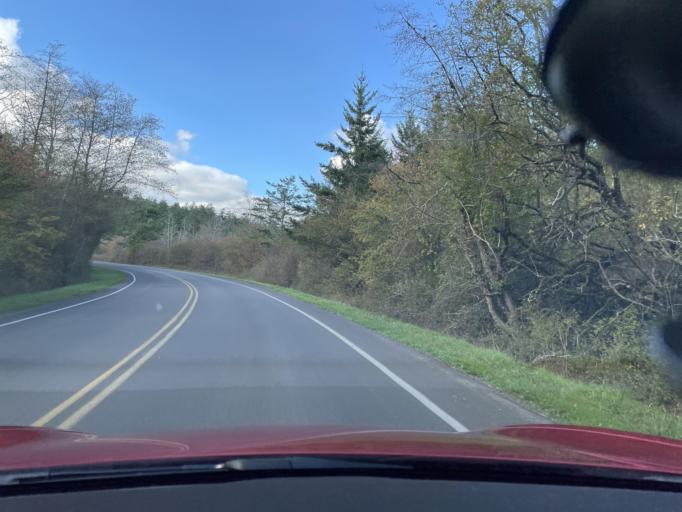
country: US
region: Washington
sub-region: San Juan County
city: Friday Harbor
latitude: 48.4680
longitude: -123.0072
